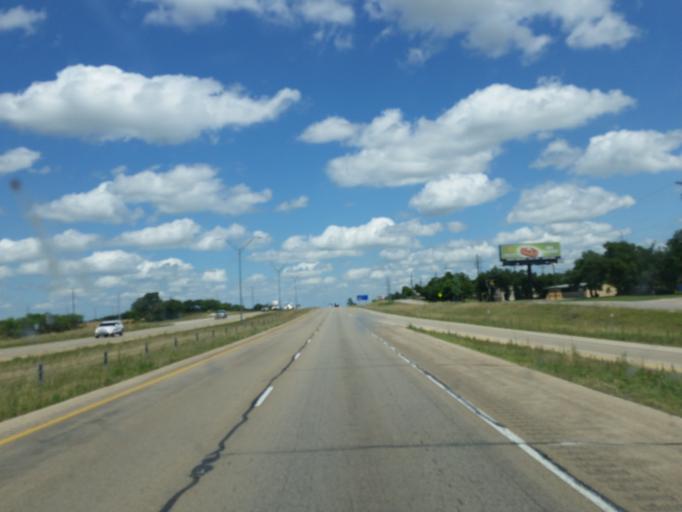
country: US
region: Texas
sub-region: Callahan County
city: Clyde
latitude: 32.4177
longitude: -99.5227
